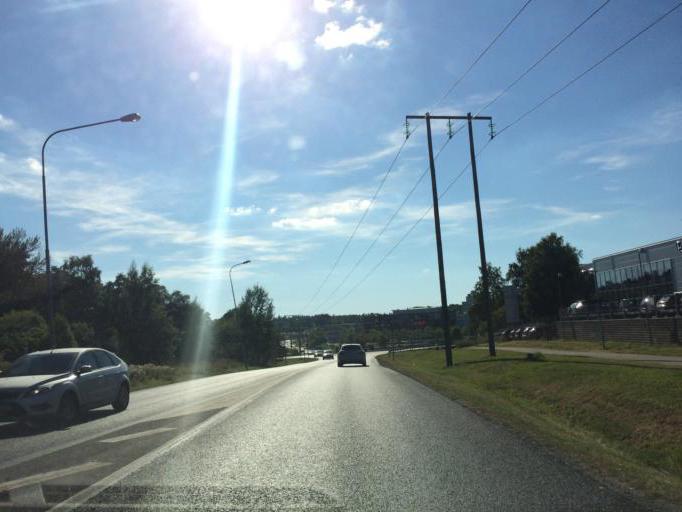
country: SE
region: Stockholm
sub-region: Upplands Vasby Kommun
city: Upplands Vaesby
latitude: 59.4990
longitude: 17.9353
